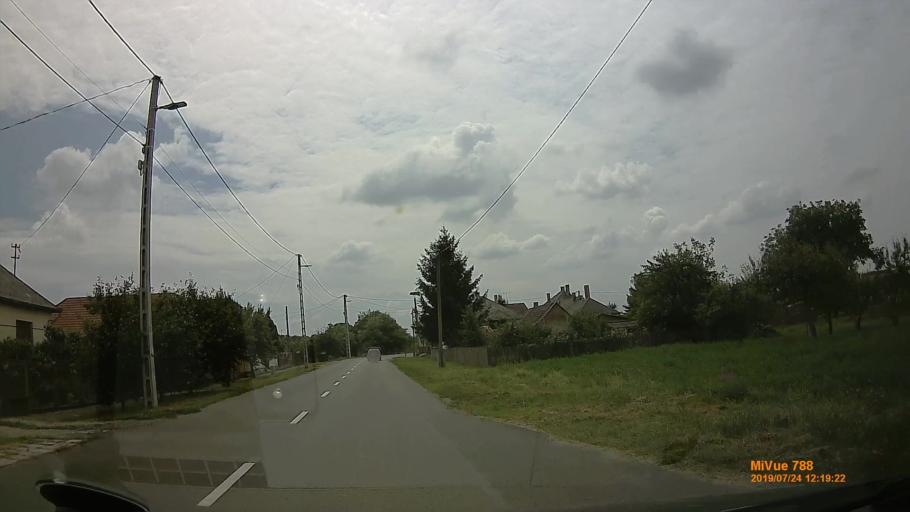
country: HU
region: Szabolcs-Szatmar-Bereg
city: Vasarosnameny
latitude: 48.1415
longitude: 22.3454
